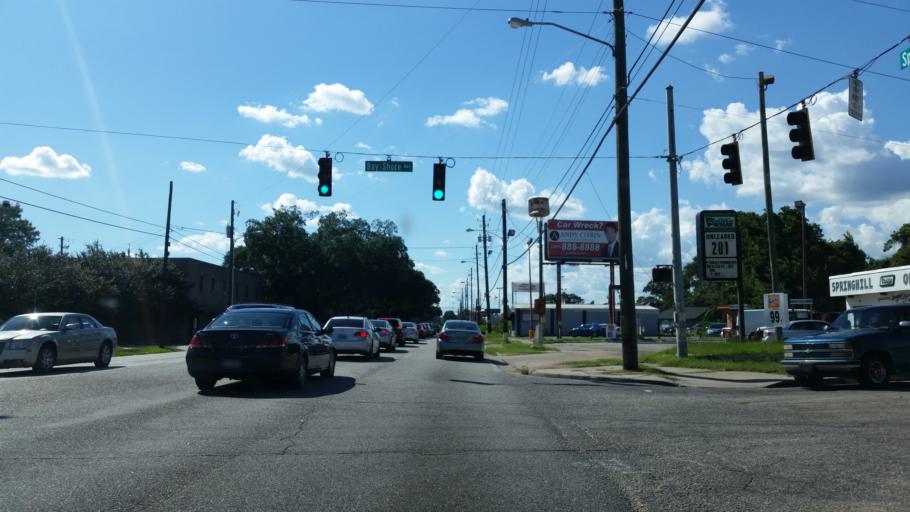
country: US
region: Alabama
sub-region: Mobile County
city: Prichard
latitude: 30.6977
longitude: -88.1061
